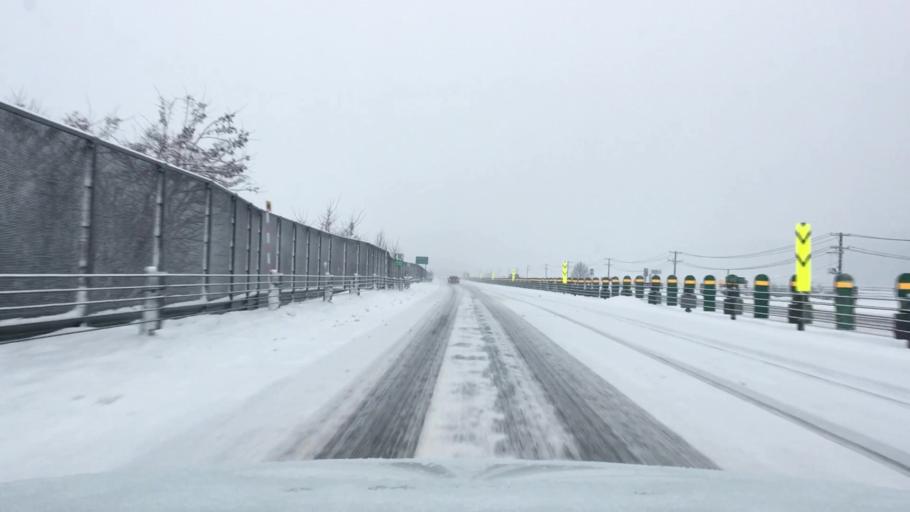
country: JP
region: Akita
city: Hanawa
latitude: 40.2800
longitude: 140.7610
